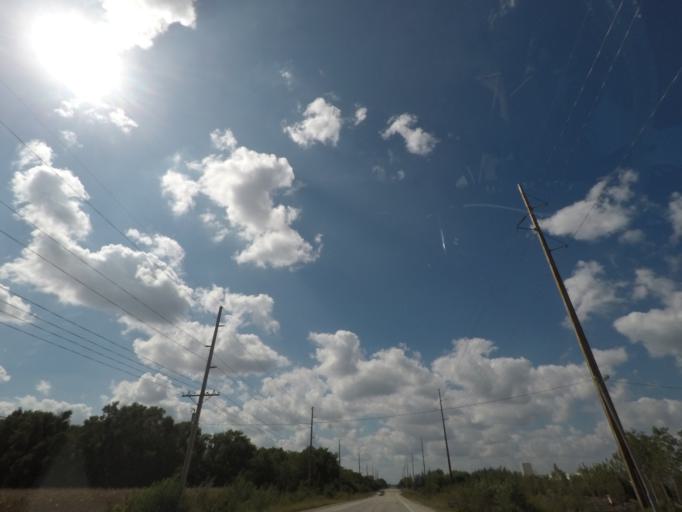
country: US
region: Iowa
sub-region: Story County
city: Ames
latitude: 42.0230
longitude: -93.5613
